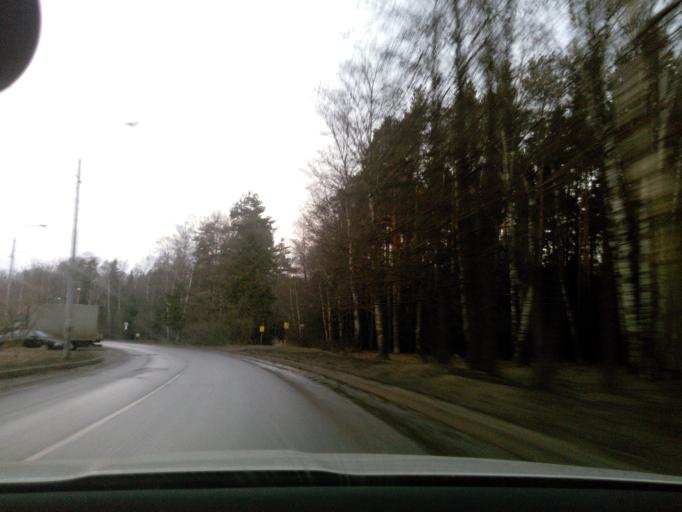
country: RU
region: Moscow
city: Zelenograd
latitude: 55.9997
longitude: 37.1883
